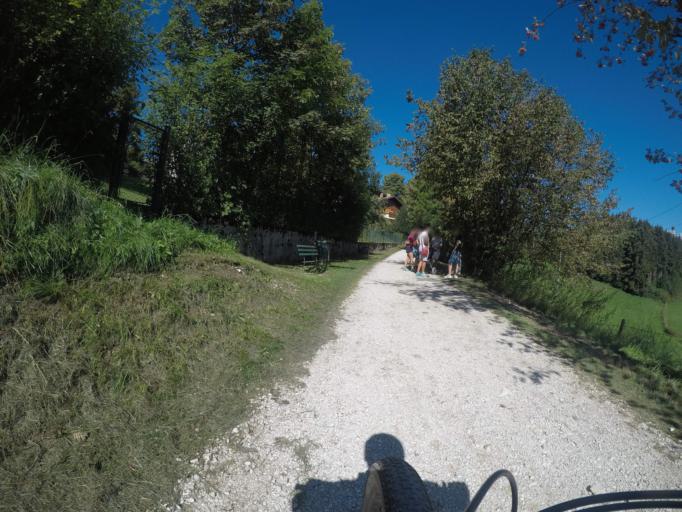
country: IT
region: Veneto
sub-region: Provincia di Vicenza
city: Canove di Roana
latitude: 45.8606
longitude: 11.4755
